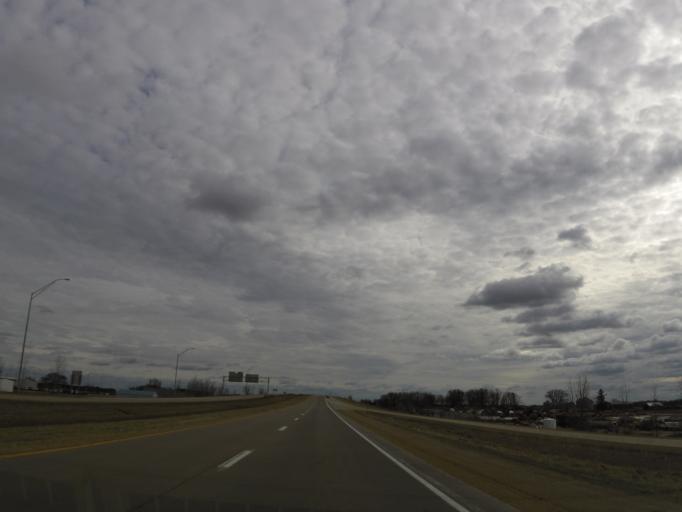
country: US
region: Iowa
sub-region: Chickasaw County
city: New Hampton
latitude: 43.0643
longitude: -92.3350
